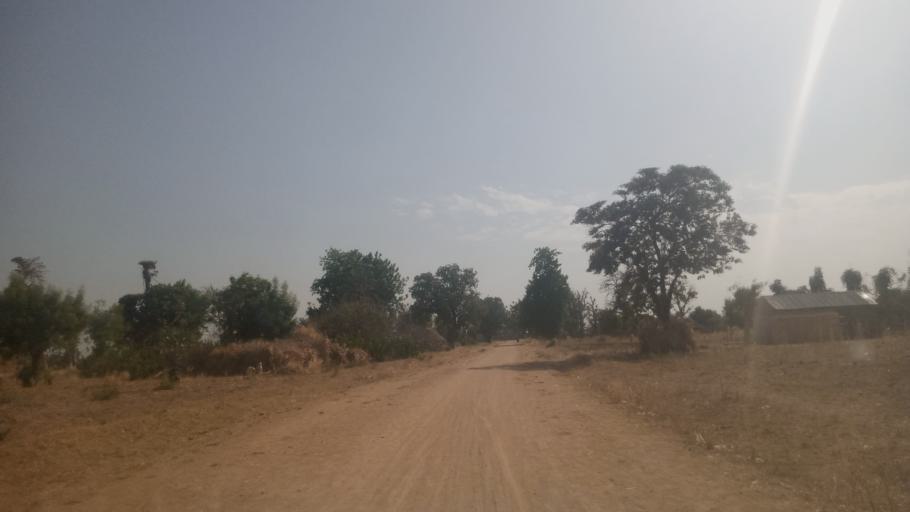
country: NG
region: Adamawa
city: Mayo Belwa
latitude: 9.0777
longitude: 12.0356
